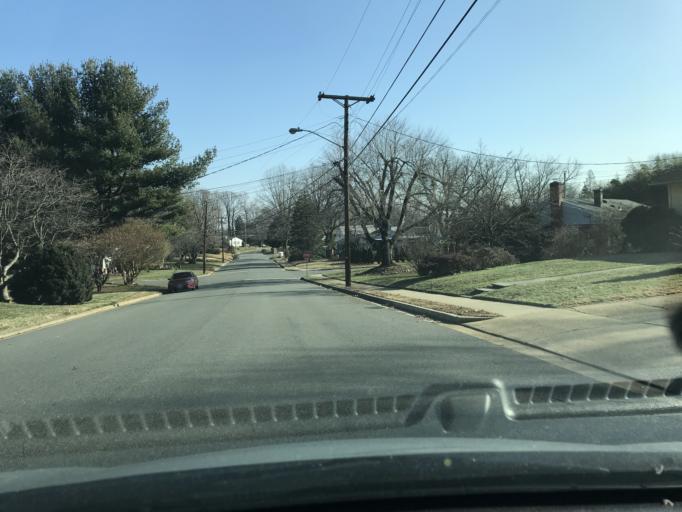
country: US
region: Virginia
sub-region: City of Fairfax
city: Fairfax
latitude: 38.8575
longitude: -77.3234
